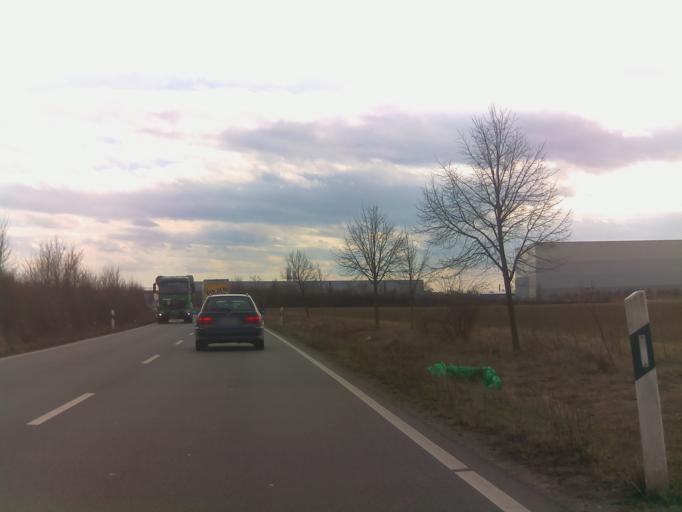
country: DE
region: Hesse
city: Biebesheim
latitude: 49.7908
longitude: 8.4852
